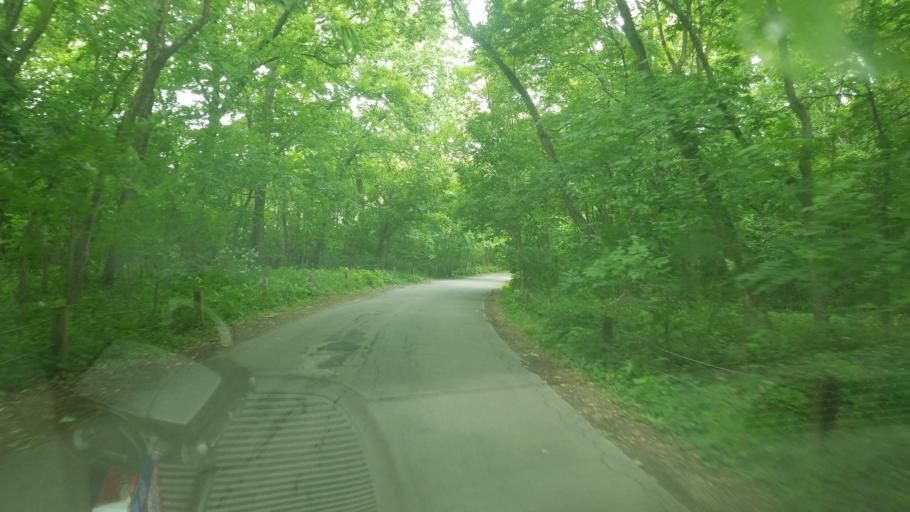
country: US
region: Ohio
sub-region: Franklin County
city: Worthington
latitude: 40.0462
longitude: -83.0182
